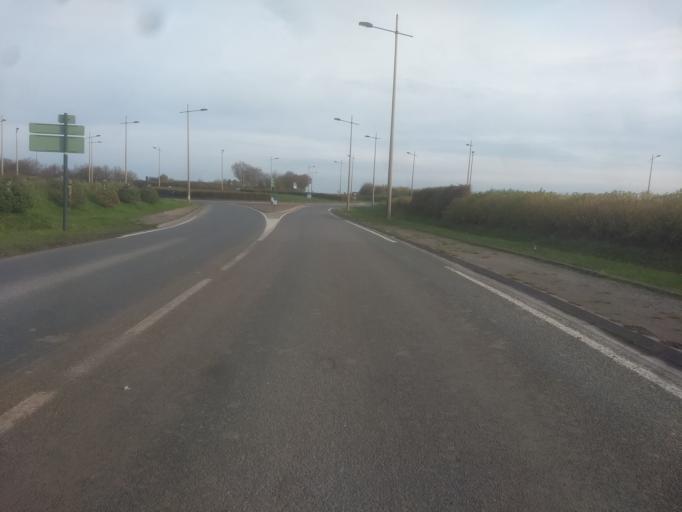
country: FR
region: Nord-Pas-de-Calais
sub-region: Departement du Pas-de-Calais
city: Agny
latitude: 50.2529
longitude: 2.7709
